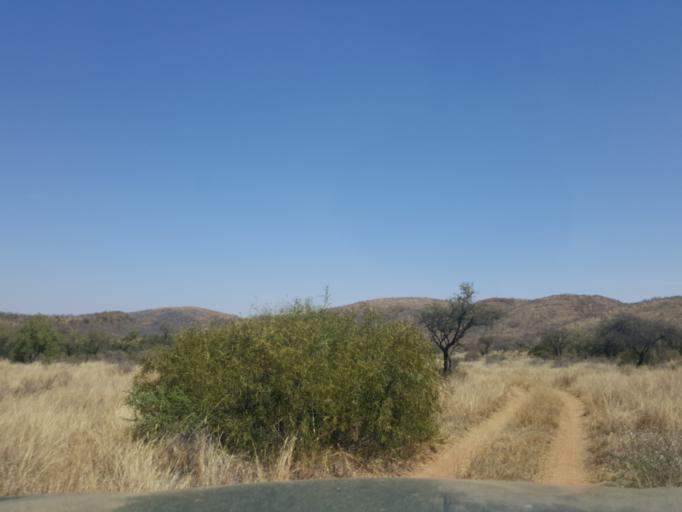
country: BW
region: South East
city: Lobatse
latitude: -25.1361
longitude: 25.6724
